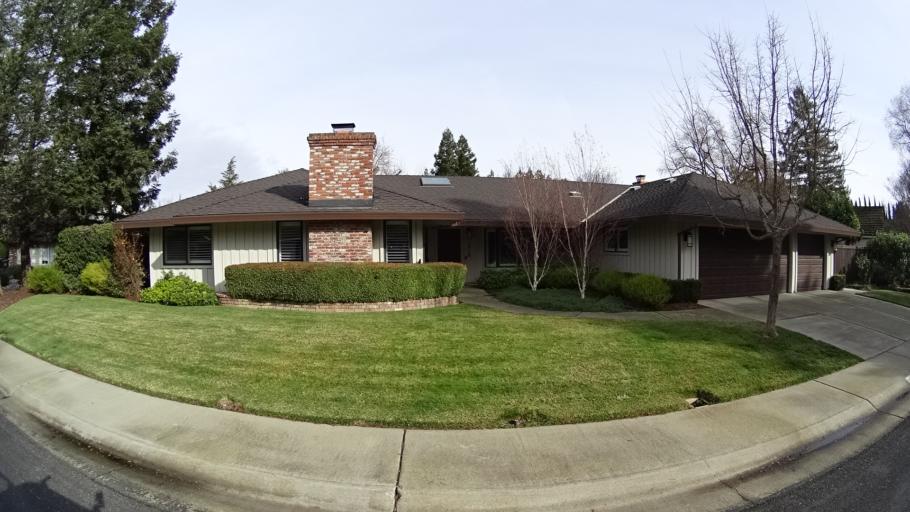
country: US
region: California
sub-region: Yolo County
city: Davis
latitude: 38.5397
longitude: -121.7014
